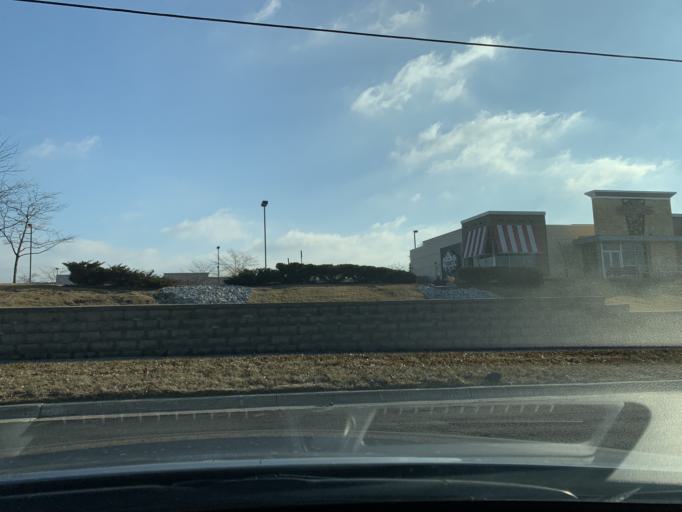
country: US
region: Indiana
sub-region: Porter County
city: Valparaiso
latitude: 41.4670
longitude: -87.0271
